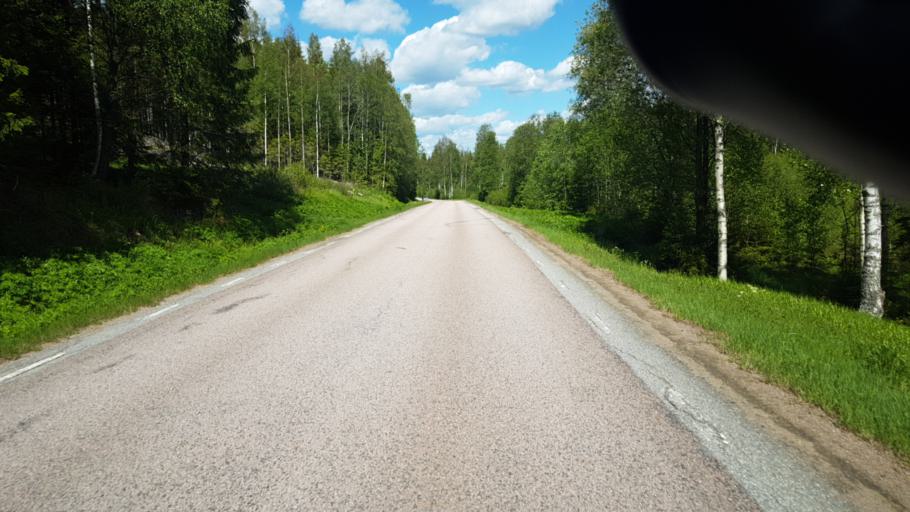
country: SE
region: Vaermland
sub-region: Arvika Kommun
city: Arvika
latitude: 59.7123
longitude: 12.7956
